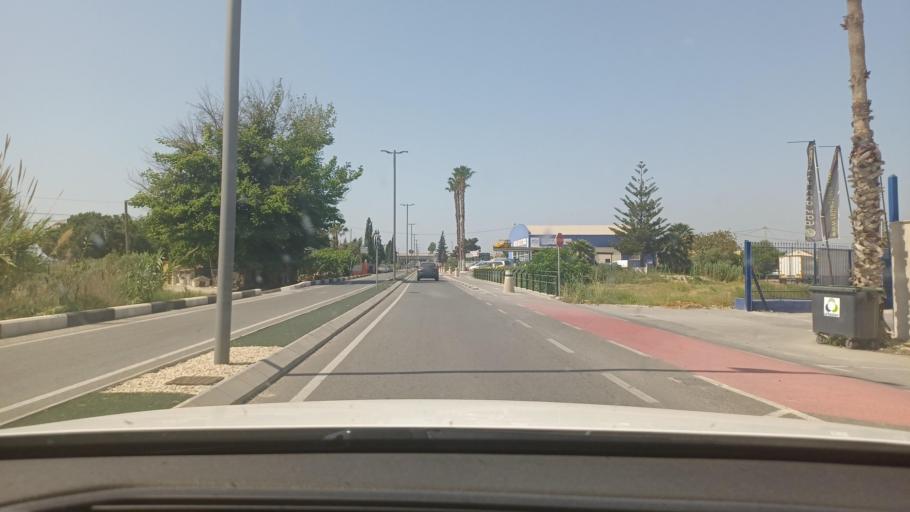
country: ES
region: Valencia
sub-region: Provincia de Alicante
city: Dolores
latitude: 38.1289
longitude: -0.7778
